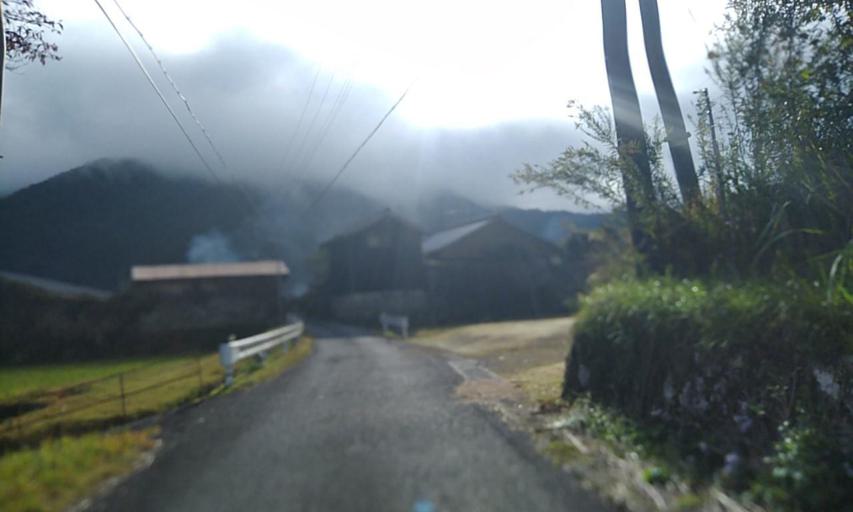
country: JP
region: Wakayama
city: Shingu
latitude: 33.9212
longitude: 135.9834
